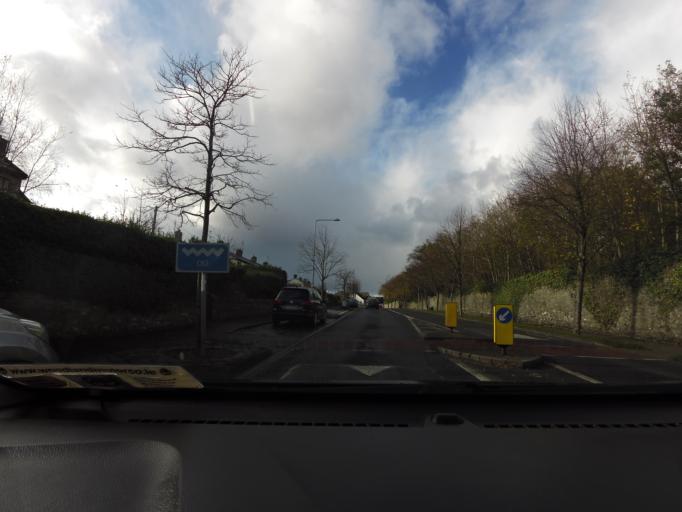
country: IE
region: Connaught
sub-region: Maigh Eo
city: Westport
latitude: 53.7980
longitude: -9.5298
